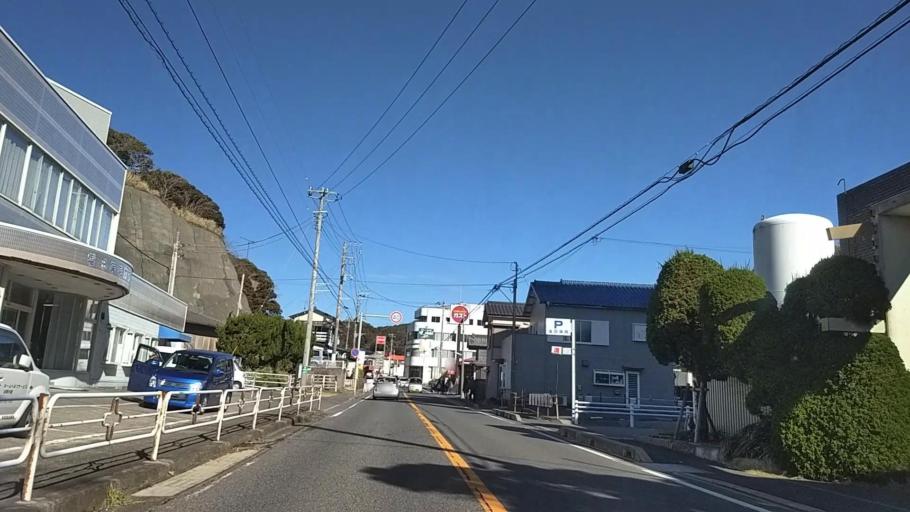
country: JP
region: Chiba
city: Katsuura
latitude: 35.1516
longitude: 140.3177
